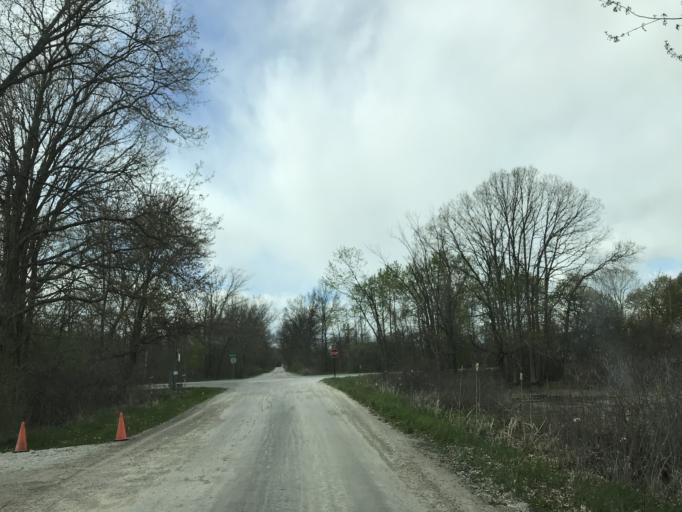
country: US
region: Michigan
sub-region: Livingston County
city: Whitmore Lake
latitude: 42.4124
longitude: -83.7240
